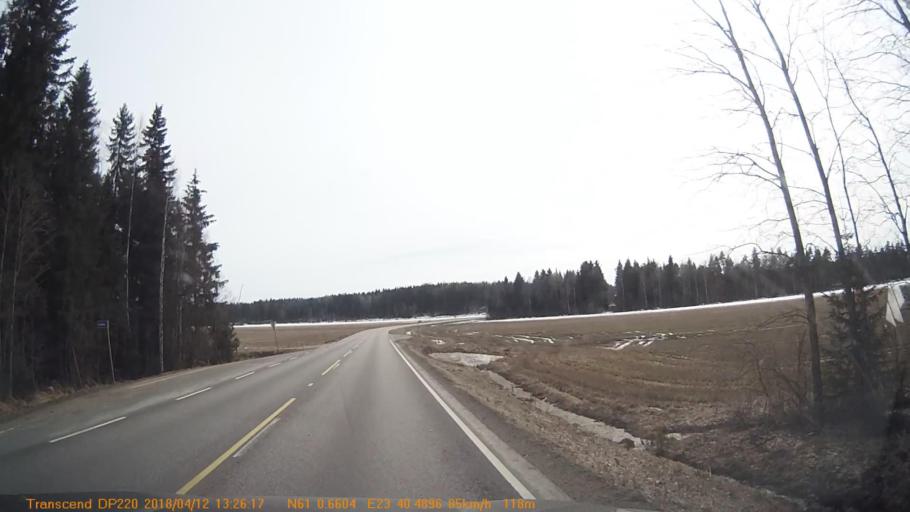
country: FI
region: Pirkanmaa
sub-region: Etelae-Pirkanmaa
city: Kylmaekoski
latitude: 61.0109
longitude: 23.6749
